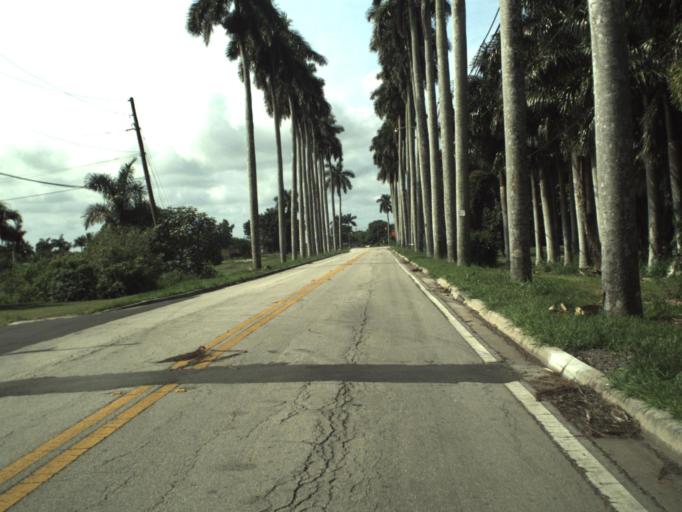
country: US
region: Florida
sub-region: Palm Beach County
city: Pahokee
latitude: 26.8002
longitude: -80.6939
